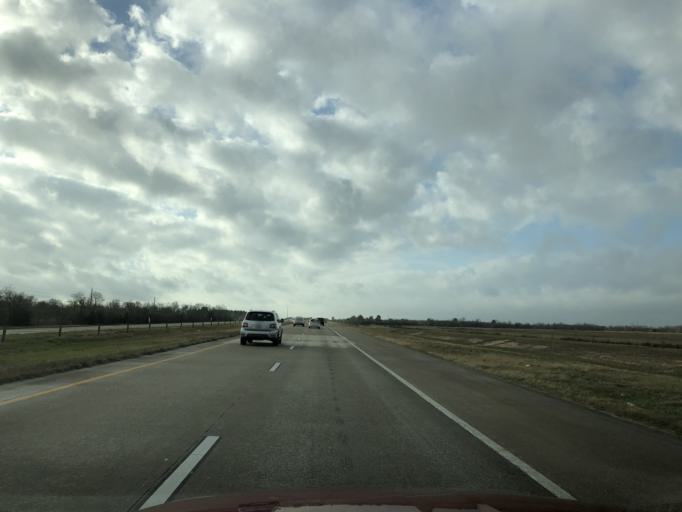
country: US
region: Texas
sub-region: Harris County
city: Cypress
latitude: 29.8968
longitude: -95.7583
